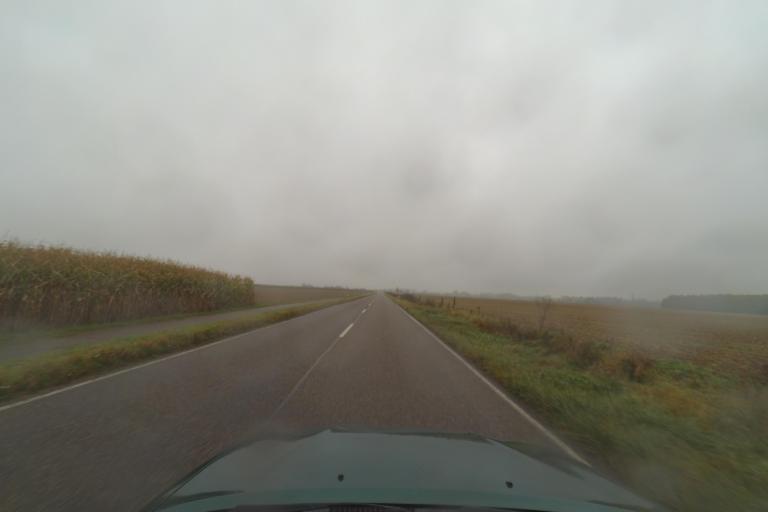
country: DE
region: Rheinland-Pfalz
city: Steinweiler
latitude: 49.1145
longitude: 8.1575
